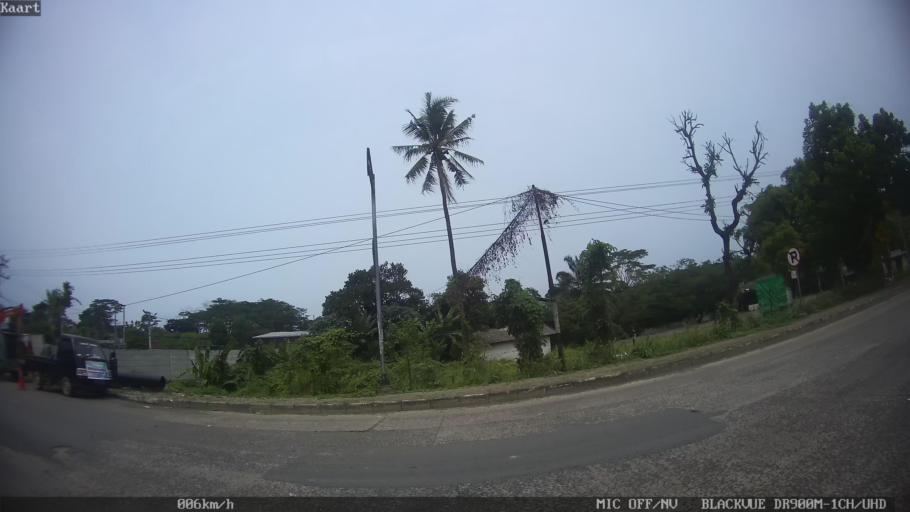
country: ID
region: Lampung
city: Bandarlampung
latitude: -5.4082
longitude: 105.2938
